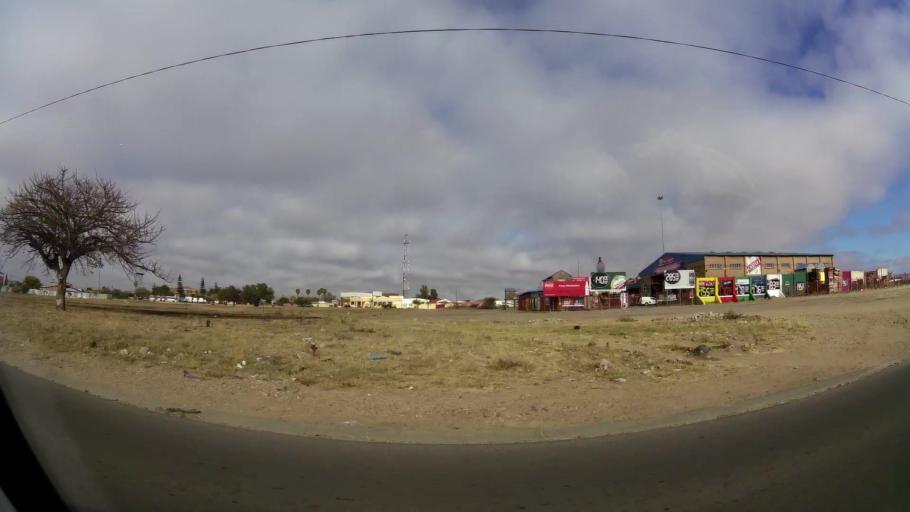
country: ZA
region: Limpopo
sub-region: Capricorn District Municipality
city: Polokwane
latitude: -23.8511
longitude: 29.3840
